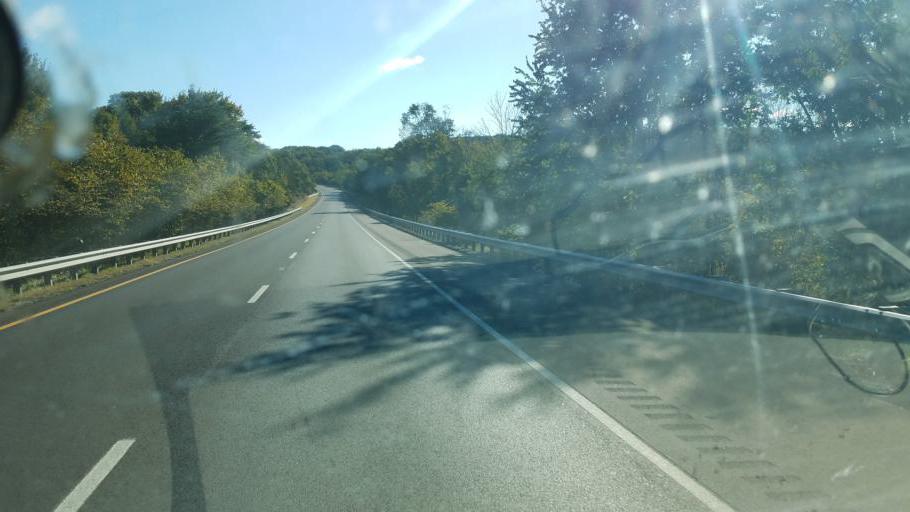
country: US
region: Maryland
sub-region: Washington County
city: Wilson-Conococheague
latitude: 39.6273
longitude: -77.9781
